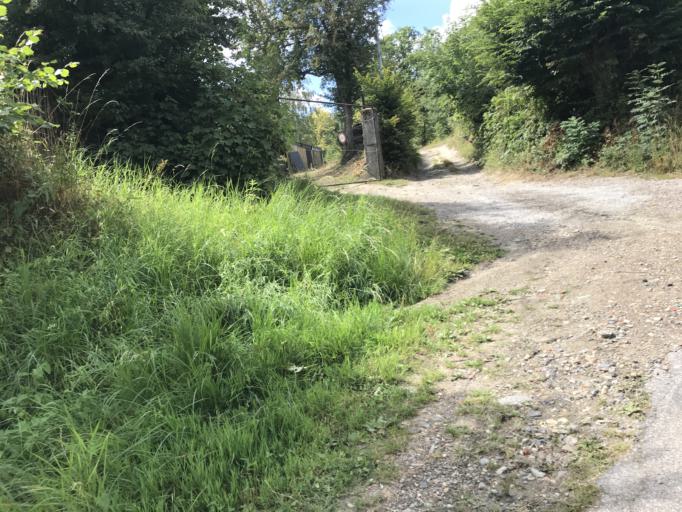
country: FR
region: Champagne-Ardenne
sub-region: Departement des Ardennes
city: Montherme
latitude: 49.8874
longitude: 4.7461
